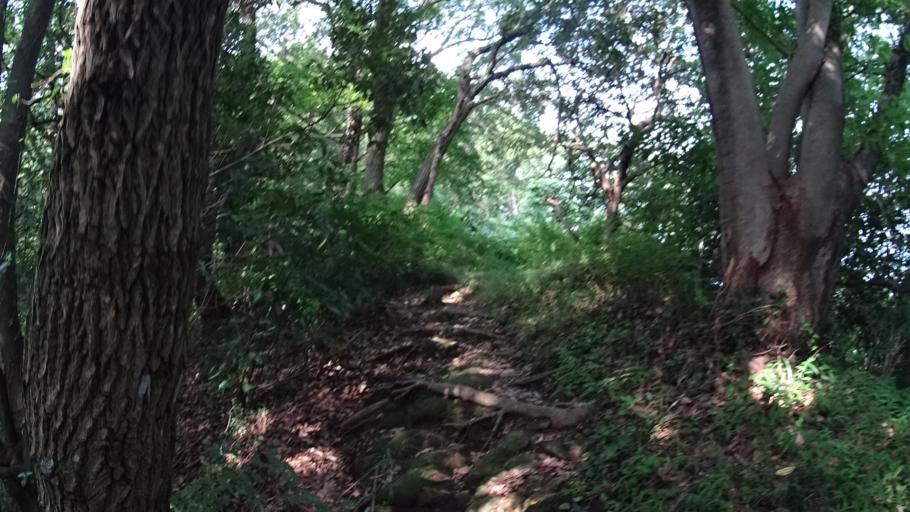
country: JP
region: Kanagawa
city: Yokosuka
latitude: 35.2821
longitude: 139.6258
